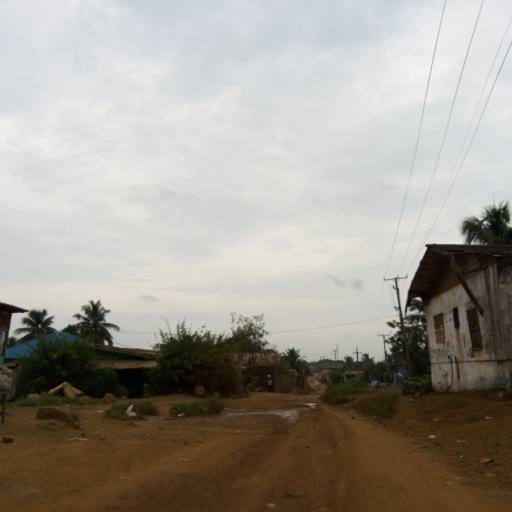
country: LR
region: Montserrado
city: Monrovia
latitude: 6.2947
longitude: -10.6789
